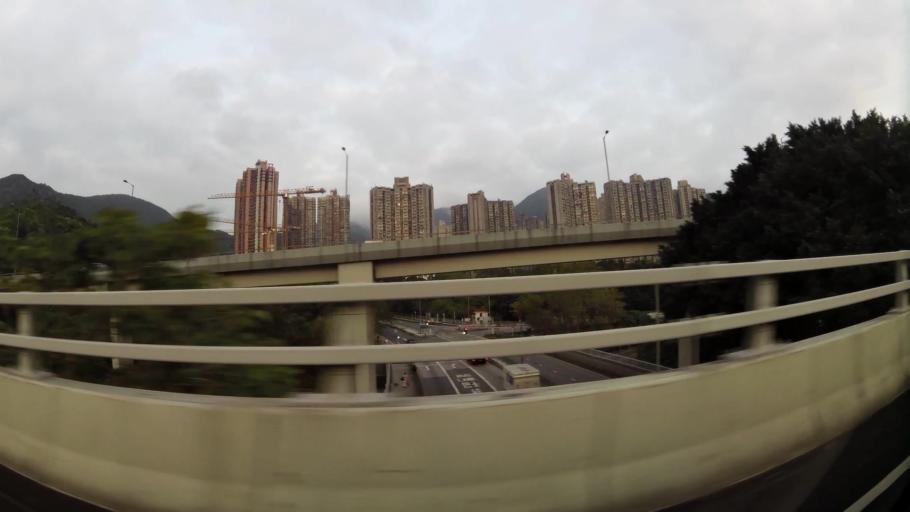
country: HK
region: Sha Tin
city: Sha Tin
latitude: 22.3829
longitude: 114.2105
